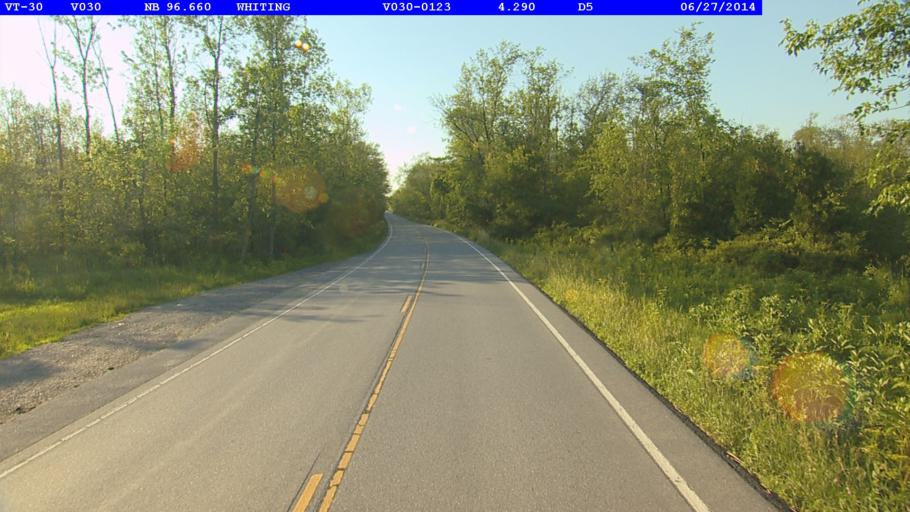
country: US
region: Vermont
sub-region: Addison County
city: Middlebury (village)
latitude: 43.8991
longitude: -73.2047
